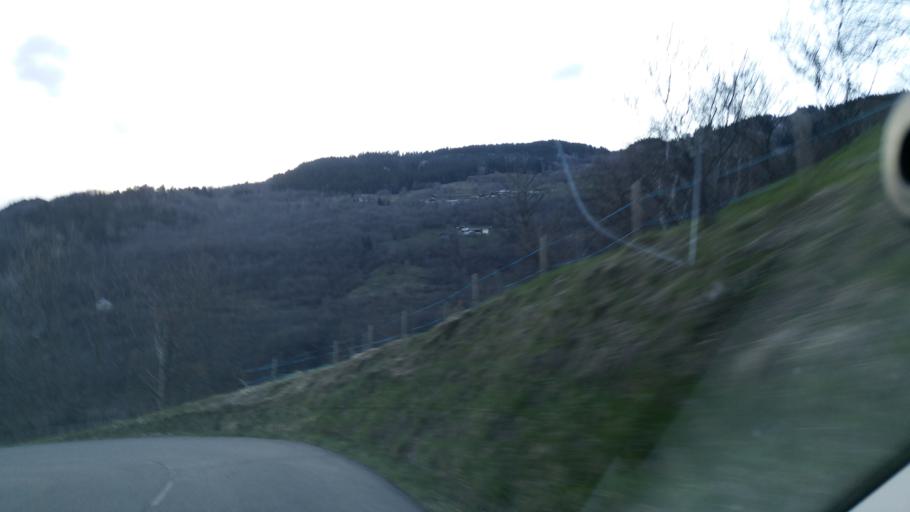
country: FR
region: Rhone-Alpes
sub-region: Departement de la Savoie
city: La Chambre
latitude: 45.3845
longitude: 6.3279
